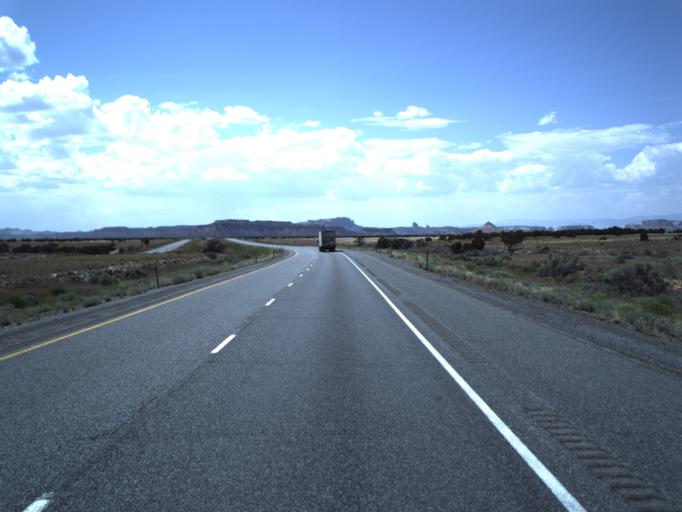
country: US
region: Utah
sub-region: Emery County
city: Castle Dale
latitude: 38.8976
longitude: -110.5952
